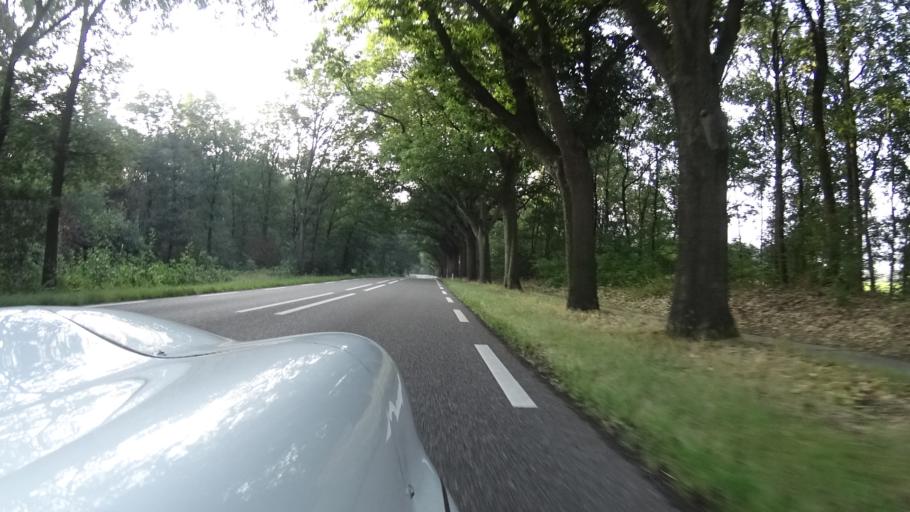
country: NL
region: Limburg
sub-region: Gemeente Bergen
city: Wellerlooi
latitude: 51.5242
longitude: 6.1423
